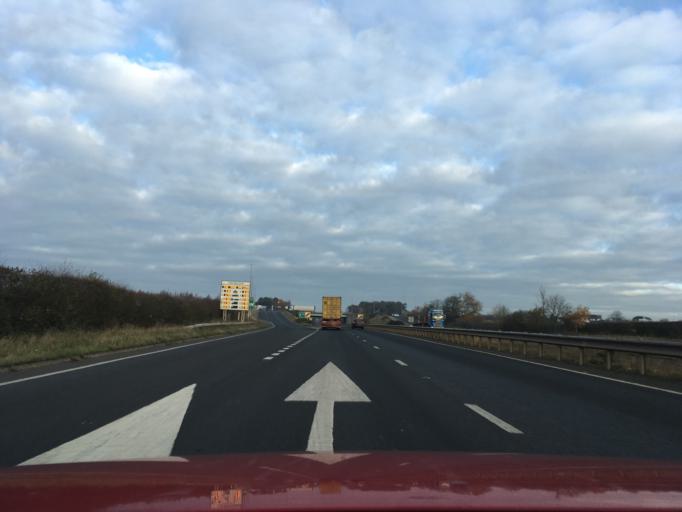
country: GB
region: England
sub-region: Staffordshire
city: Shenstone
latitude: 52.6354
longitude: -1.8028
